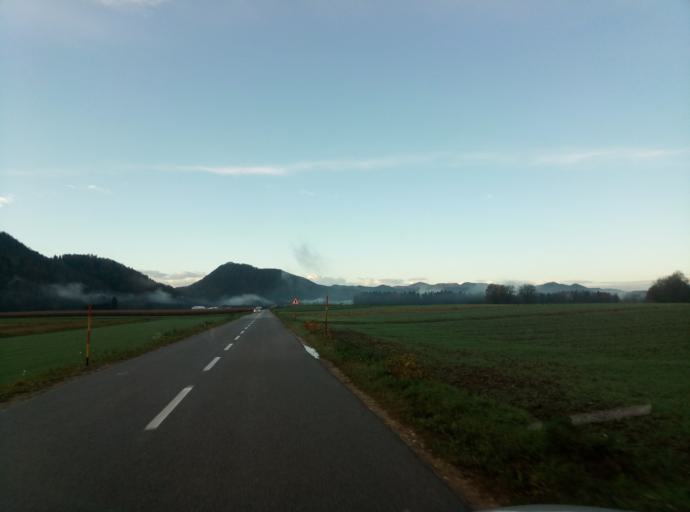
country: SI
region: Vodice
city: Vodice
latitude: 46.1570
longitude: 14.5014
